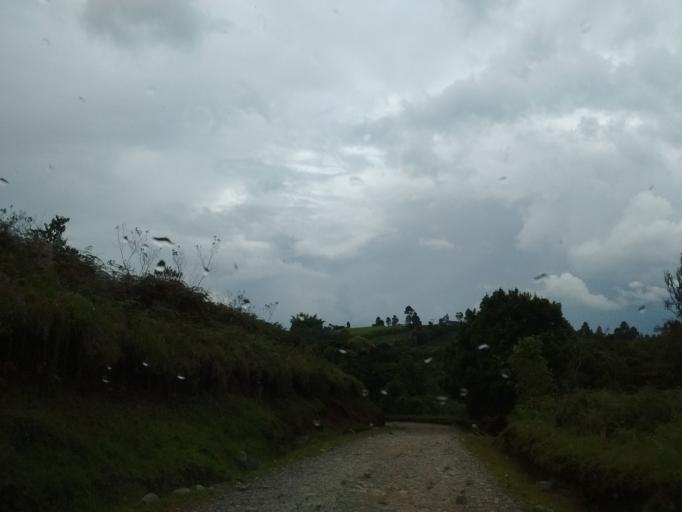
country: CO
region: Cauca
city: Cajibio
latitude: 2.5769
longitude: -76.6607
